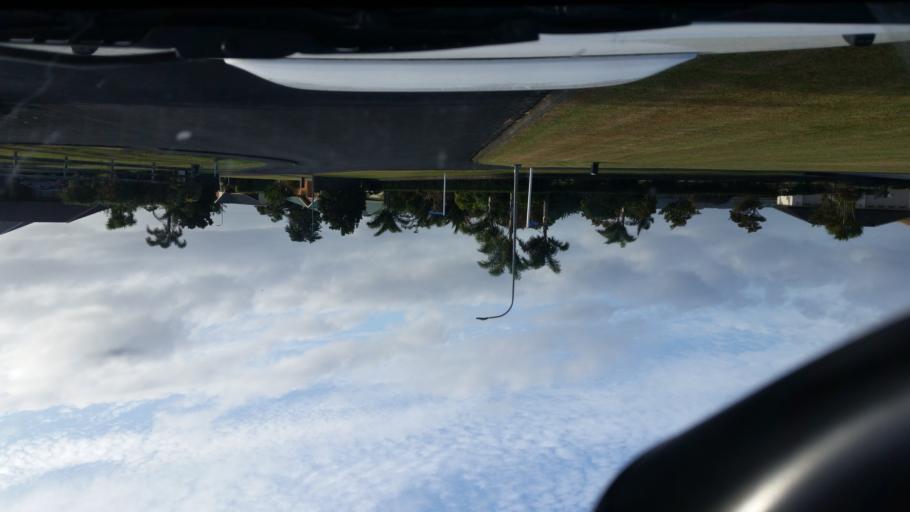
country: NZ
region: Northland
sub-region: Kaipara District
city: Dargaville
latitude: -35.9283
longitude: 173.8644
